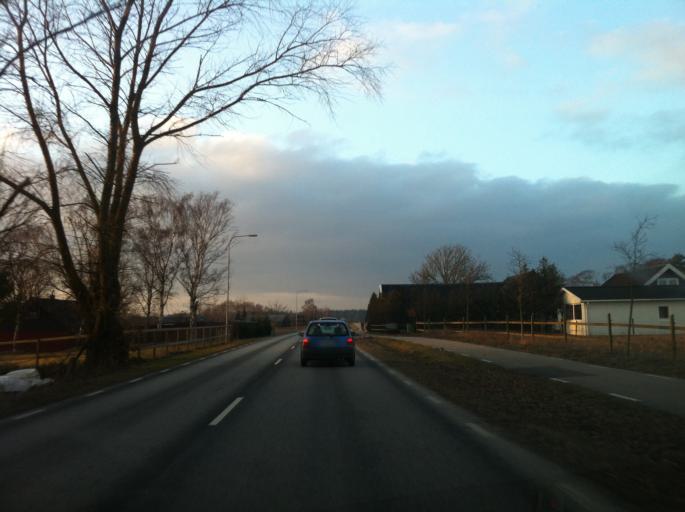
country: SE
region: Skane
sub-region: Kavlinge Kommun
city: Loddekopinge
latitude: 55.7892
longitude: 13.0007
